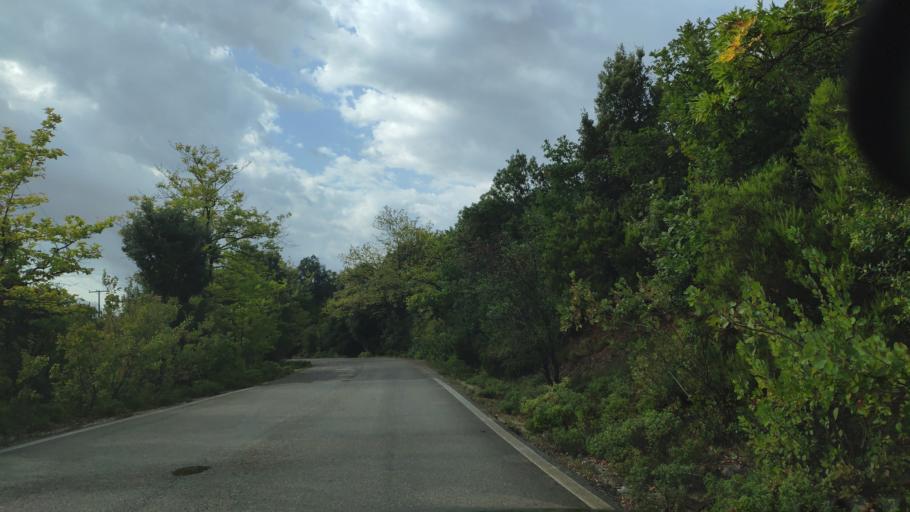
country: GR
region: West Greece
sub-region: Nomos Aitolias kai Akarnanias
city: Sardinia
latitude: 38.8579
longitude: 21.3062
